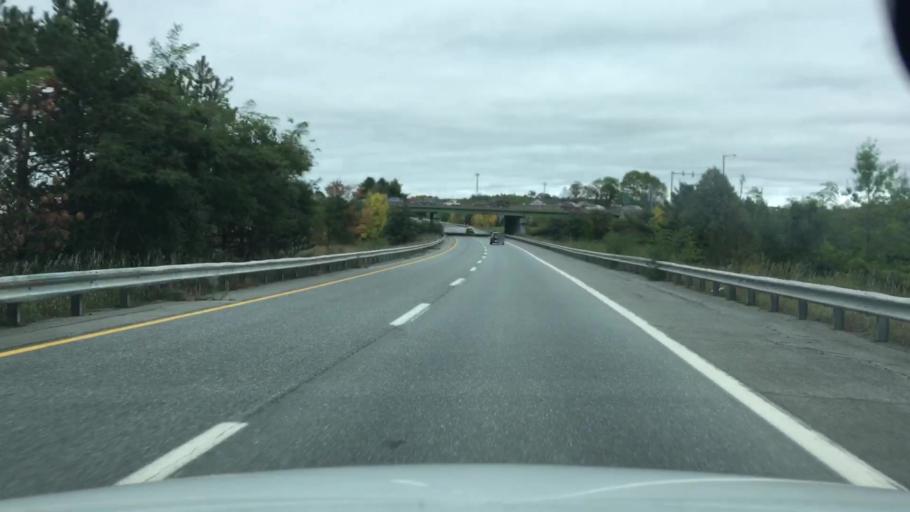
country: US
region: Maine
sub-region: Penobscot County
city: Veazie
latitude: 44.8307
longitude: -68.7430
